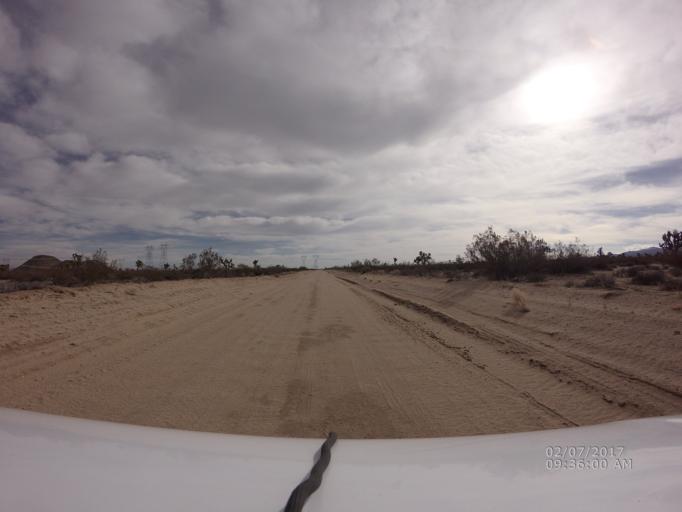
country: US
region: California
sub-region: San Bernardino County
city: Pinon Hills
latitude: 34.5276
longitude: -117.7177
